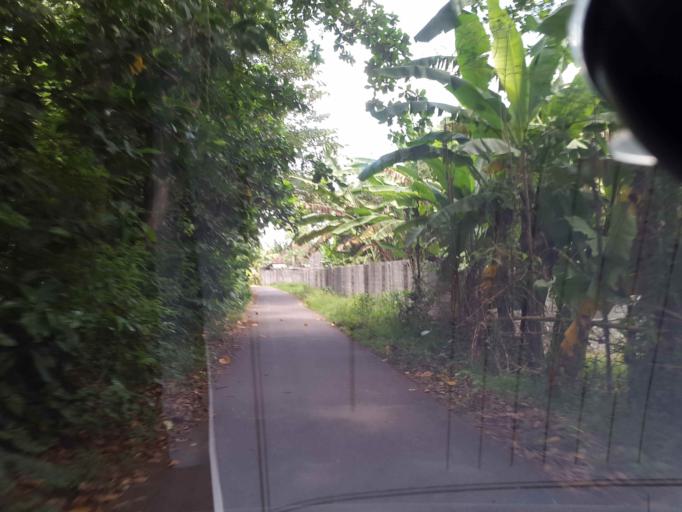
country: ID
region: West Nusa Tenggara
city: Jelateng Timur
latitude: -8.6937
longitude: 116.0759
